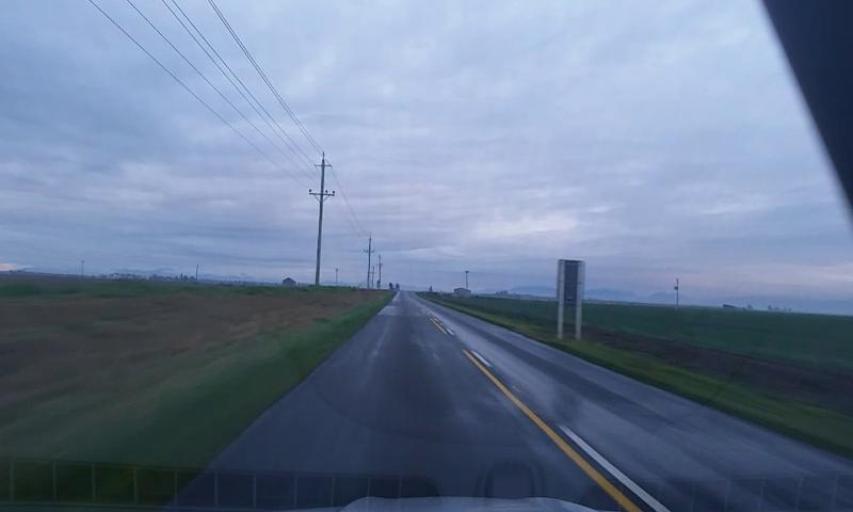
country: NZ
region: Canterbury
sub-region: Ashburton District
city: Rakaia
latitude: -43.7554
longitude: 171.9214
